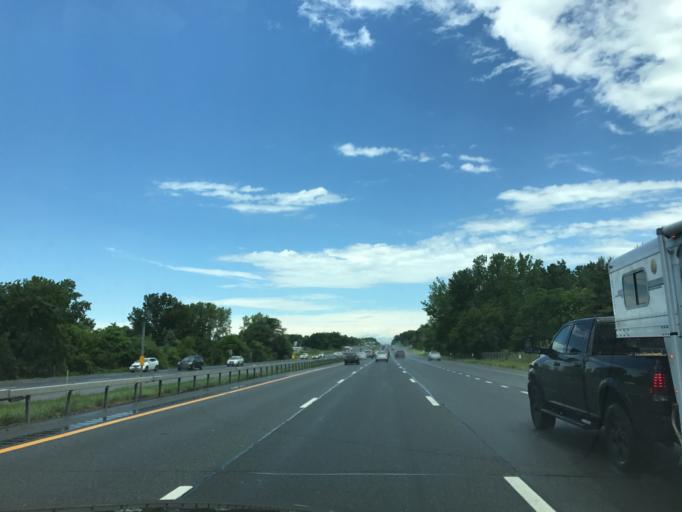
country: US
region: New York
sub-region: Saratoga County
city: Country Knolls
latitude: 42.8541
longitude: -73.7737
